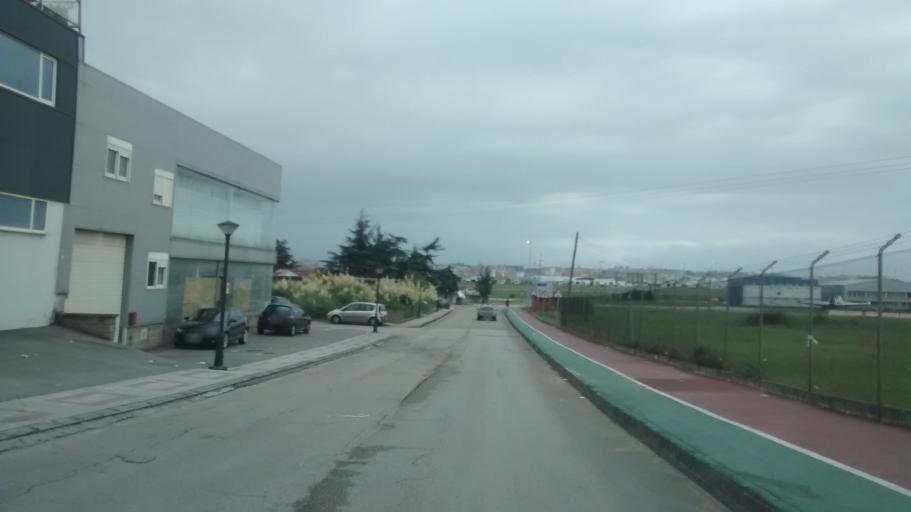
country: ES
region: Cantabria
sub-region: Provincia de Cantabria
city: El Astillero
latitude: 43.4222
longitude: -3.8288
